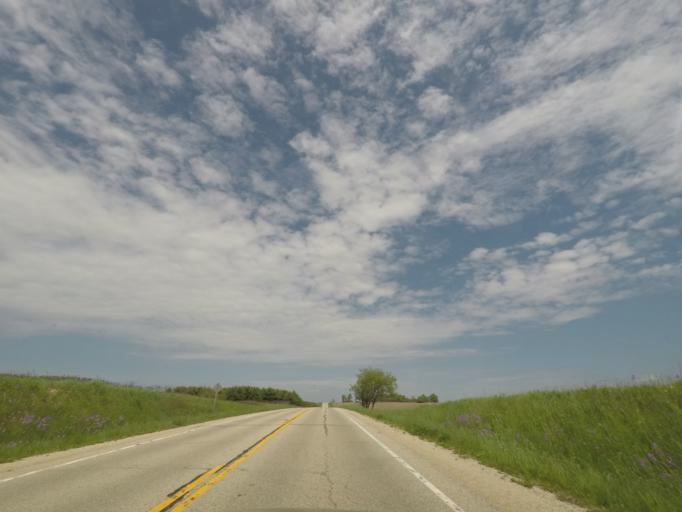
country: US
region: Wisconsin
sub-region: Rock County
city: Orfordville
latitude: 42.6603
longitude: -89.2885
